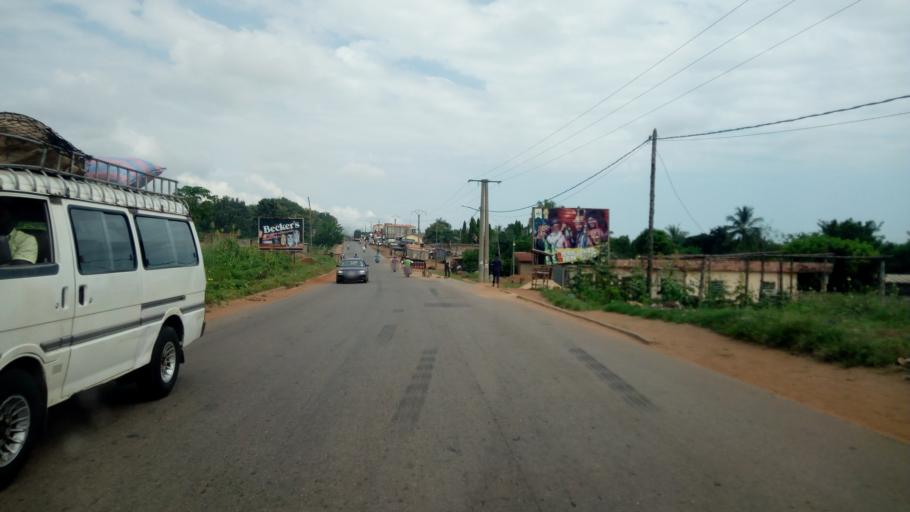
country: TG
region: Plateaux
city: Atakpame
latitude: 7.5040
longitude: 1.1551
